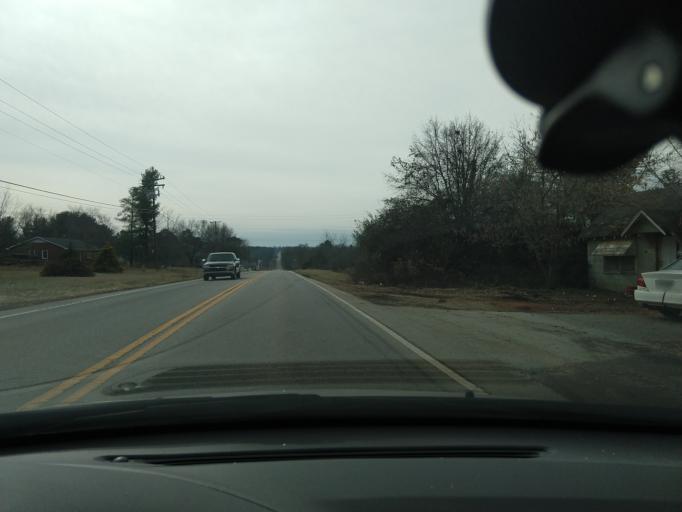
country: US
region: South Carolina
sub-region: Spartanburg County
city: Cowpens
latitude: 35.0044
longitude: -81.8741
